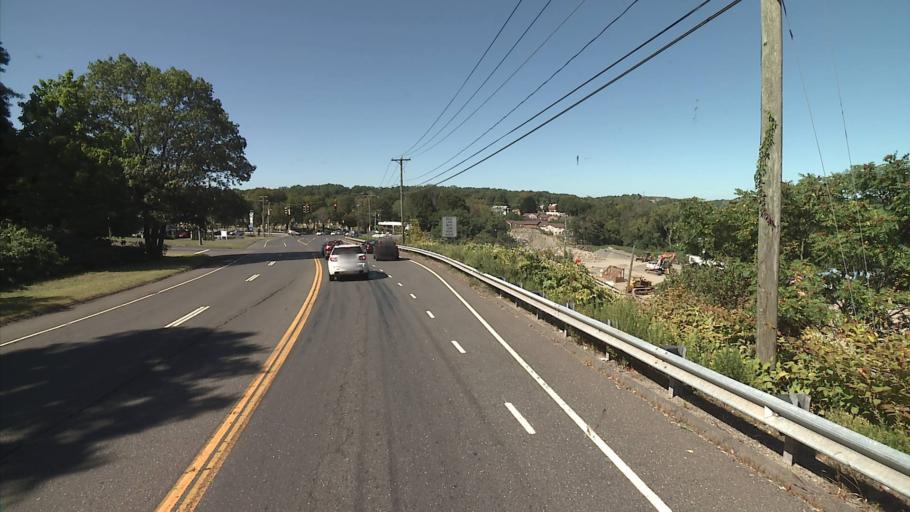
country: US
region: Connecticut
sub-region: New Haven County
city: Waterbury
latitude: 41.5368
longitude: -73.0151
